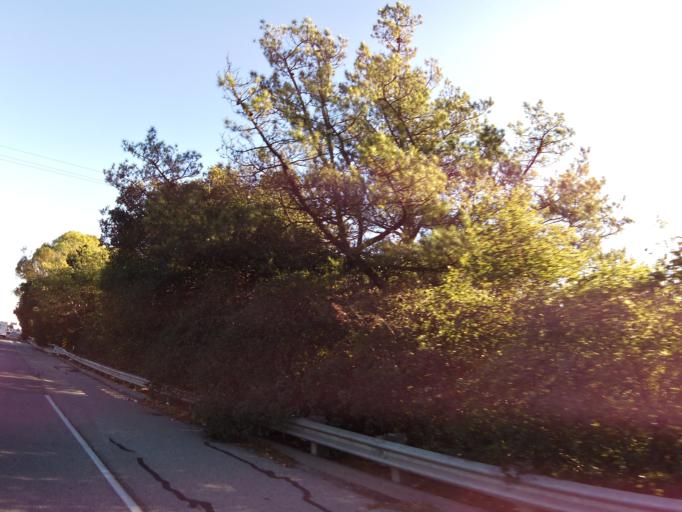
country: US
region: California
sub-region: Santa Clara County
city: Loyola
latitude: 37.3410
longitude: -122.0906
